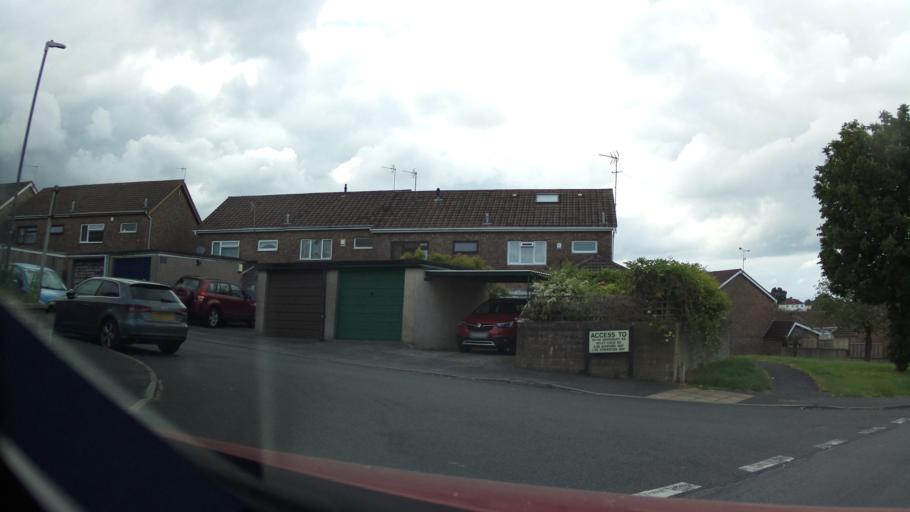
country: GB
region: England
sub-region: South Gloucestershire
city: Kingswood
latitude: 51.4557
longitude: -2.4878
